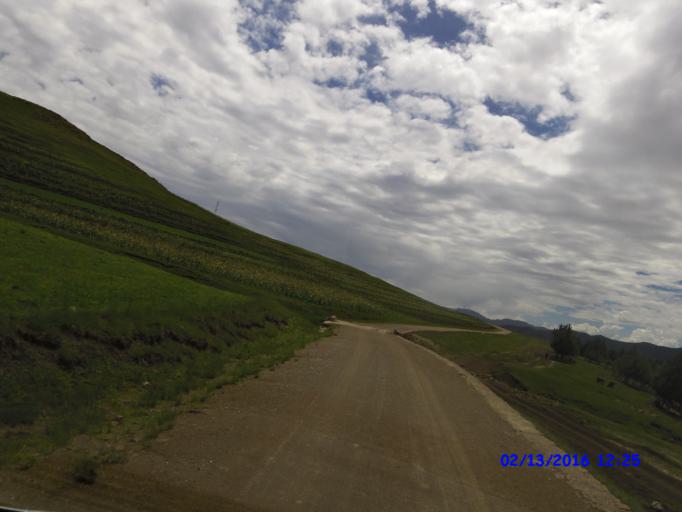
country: LS
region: Maseru
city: Nako
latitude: -29.8772
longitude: 28.0430
